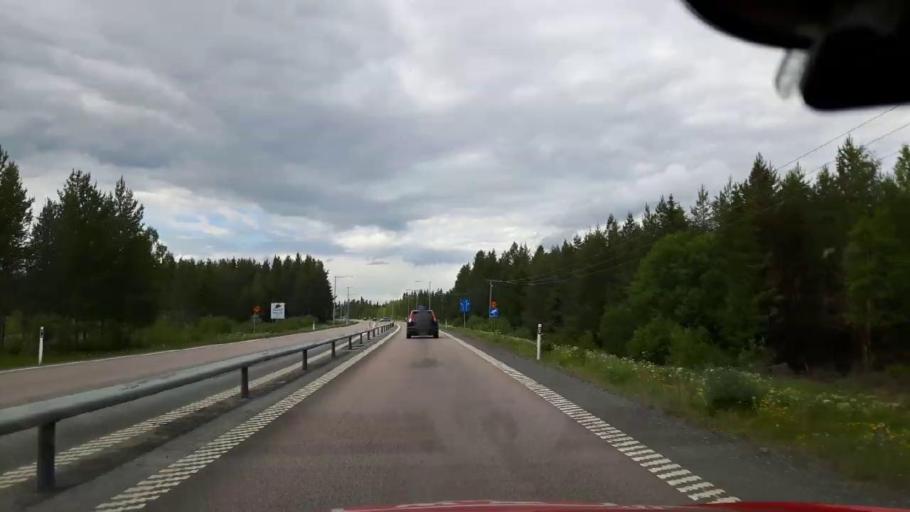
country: SE
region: Jaemtland
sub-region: OEstersunds Kommun
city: Ostersund
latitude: 63.2461
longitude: 14.5953
